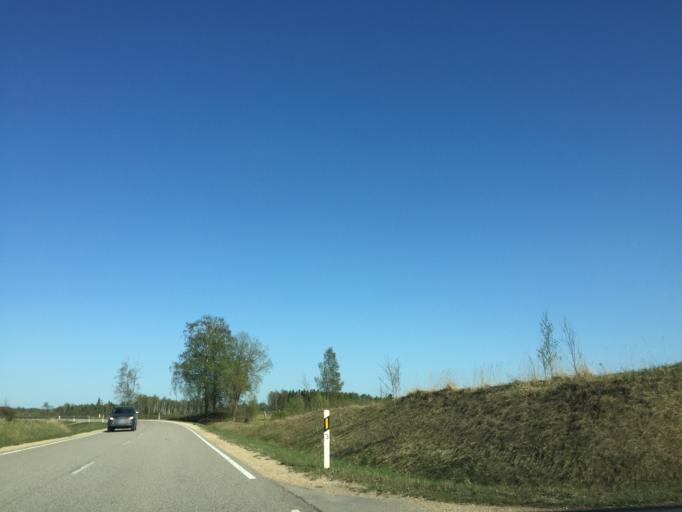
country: LV
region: Ergli
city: Ergli
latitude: 56.8994
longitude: 25.4719
